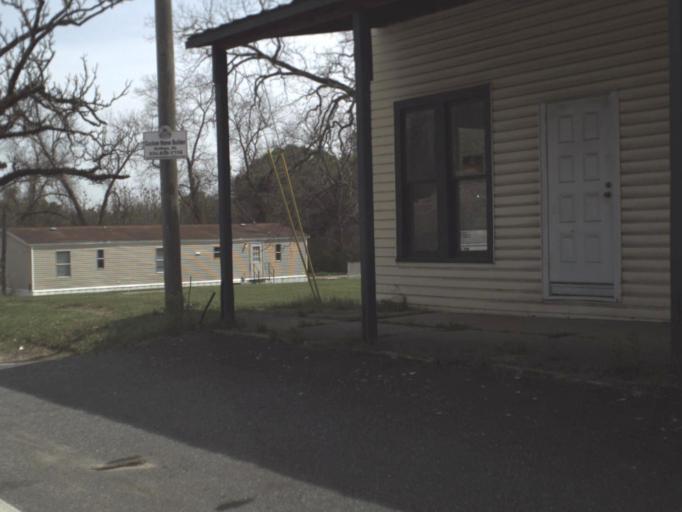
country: US
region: Florida
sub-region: Jackson County
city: Graceville
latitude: 30.9502
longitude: -85.4016
